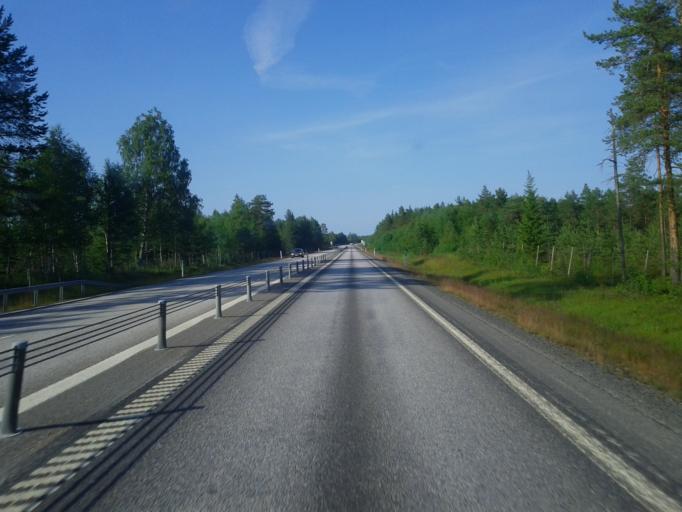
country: SE
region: Vaesterbotten
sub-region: Umea Kommun
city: Saevar
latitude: 63.9451
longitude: 20.6561
